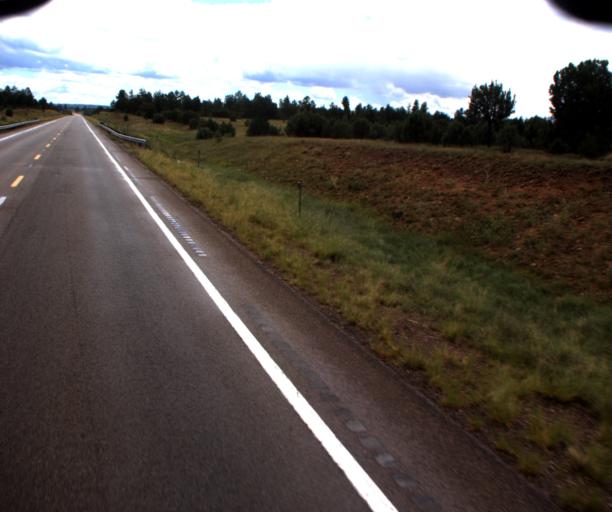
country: US
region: Arizona
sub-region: Navajo County
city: Heber-Overgaard
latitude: 34.3775
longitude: -110.4669
